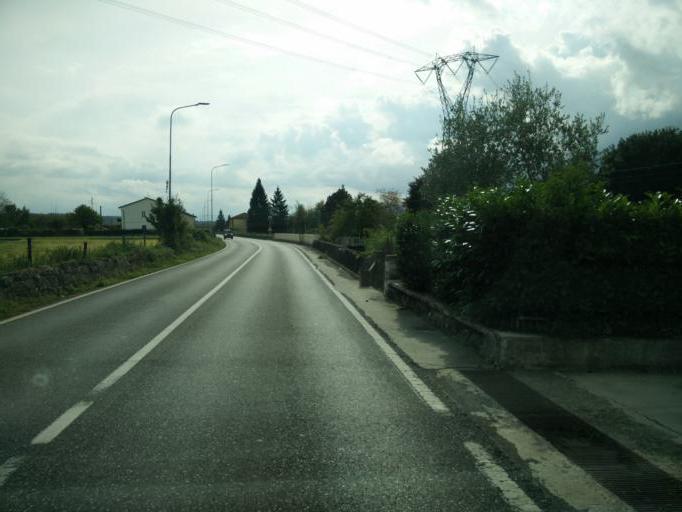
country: IT
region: Tuscany
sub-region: Provincia di Massa-Carrara
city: Pontremoli
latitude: 44.3561
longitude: 9.9033
